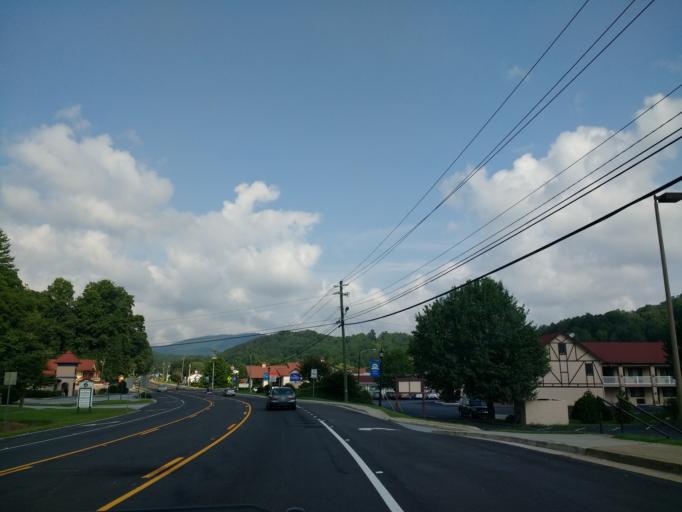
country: US
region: Georgia
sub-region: White County
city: Cleveland
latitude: 34.6995
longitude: -83.7227
